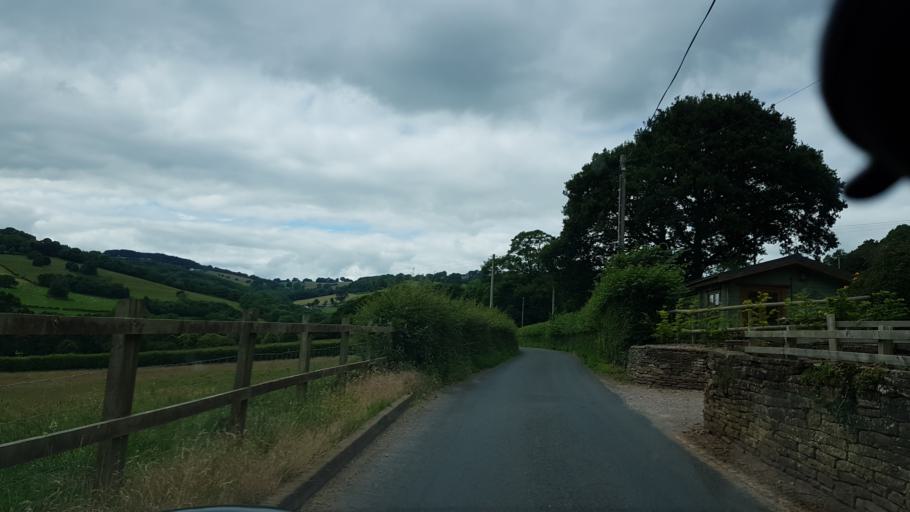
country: GB
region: England
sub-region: Herefordshire
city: Llanrothal
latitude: 51.8846
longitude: -2.8188
